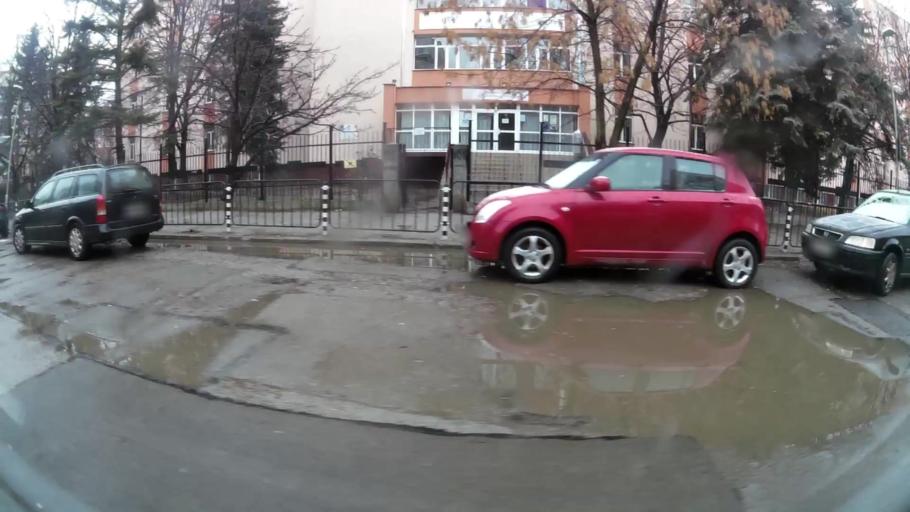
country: BG
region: Sofia-Capital
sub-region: Stolichna Obshtina
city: Sofia
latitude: 42.6697
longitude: 23.3874
